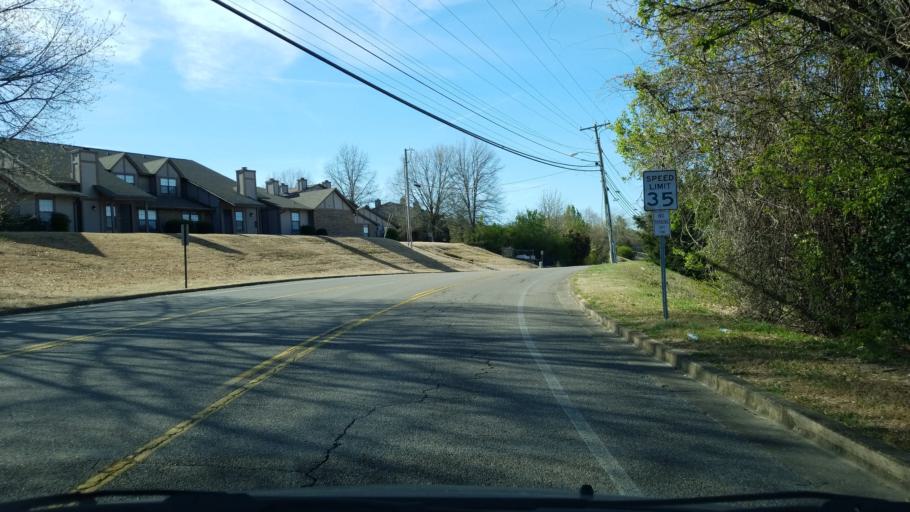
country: US
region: Tennessee
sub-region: Hamilton County
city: East Brainerd
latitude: 35.0520
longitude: -85.1803
